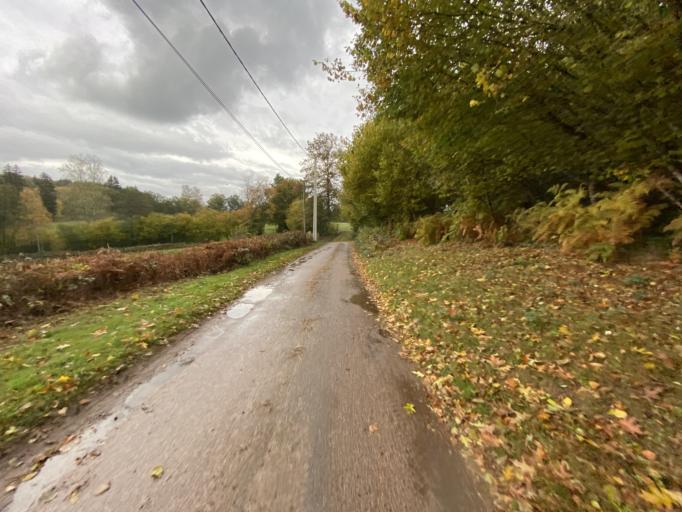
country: FR
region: Bourgogne
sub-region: Departement de la Cote-d'Or
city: Saulieu
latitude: 47.2957
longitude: 4.1231
